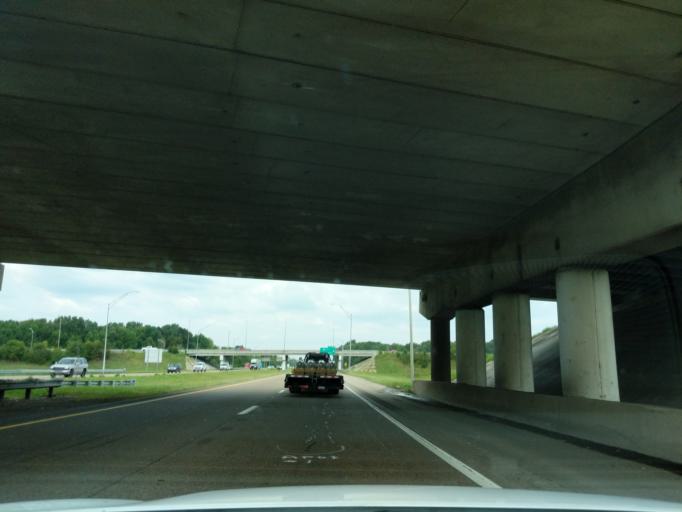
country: US
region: Tennessee
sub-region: Shelby County
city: New South Memphis
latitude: 35.0724
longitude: -90.0254
